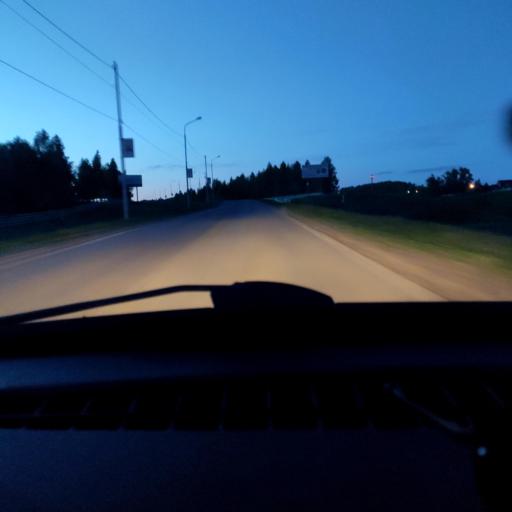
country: RU
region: Bashkortostan
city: Karmaskaly
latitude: 54.3745
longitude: 56.1747
